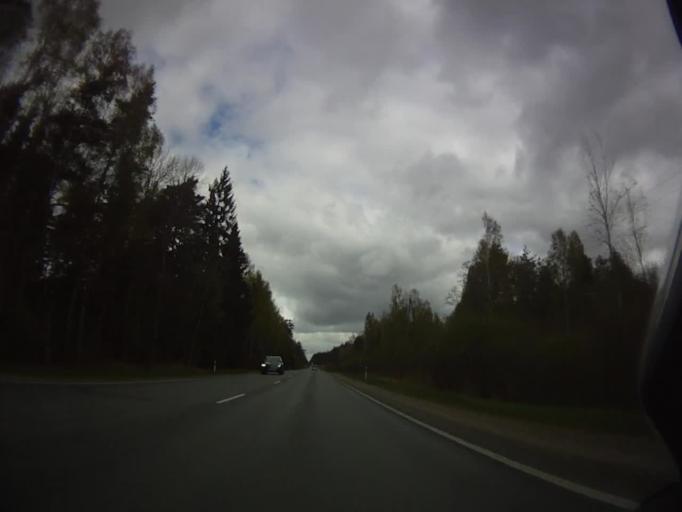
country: LV
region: Pargaujas
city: Stalbe
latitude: 57.3047
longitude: 24.9251
